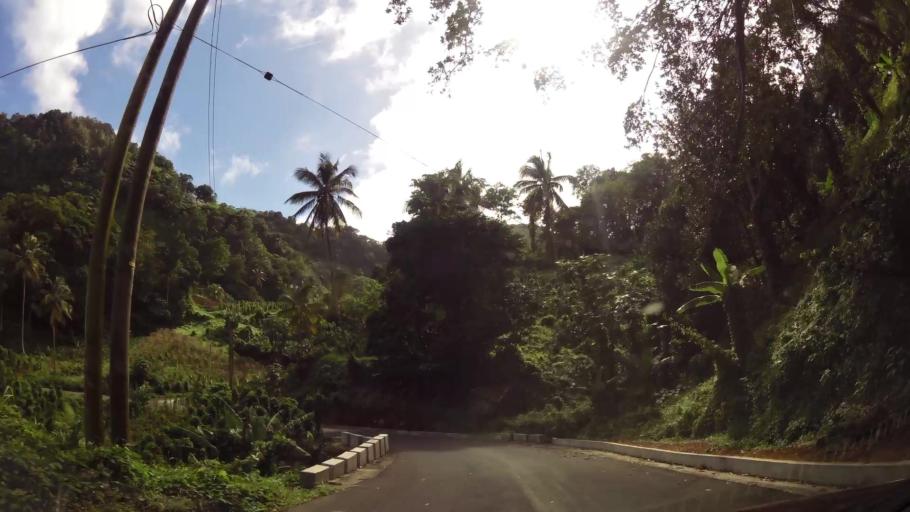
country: DM
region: Saint John
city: Portsmouth
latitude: 15.6260
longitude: -61.4276
